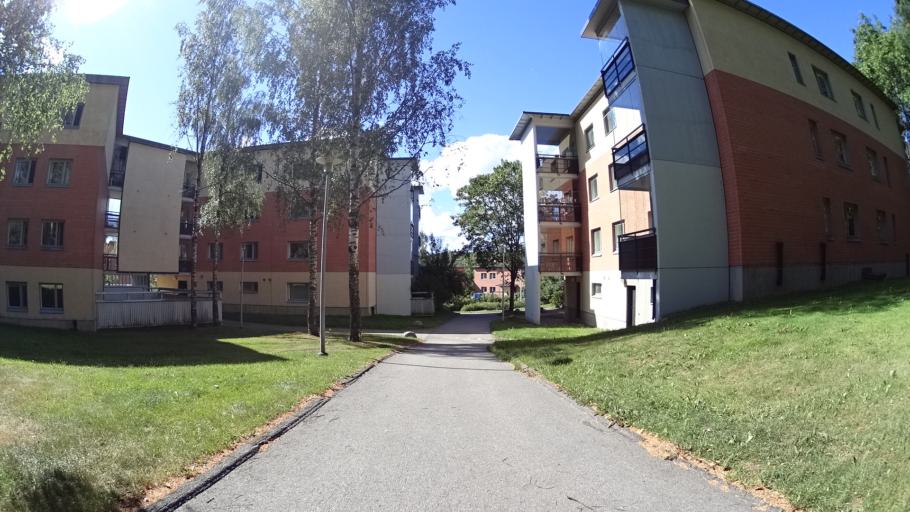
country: FI
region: Uusimaa
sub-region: Helsinki
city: Teekkarikylae
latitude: 60.2470
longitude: 24.8561
